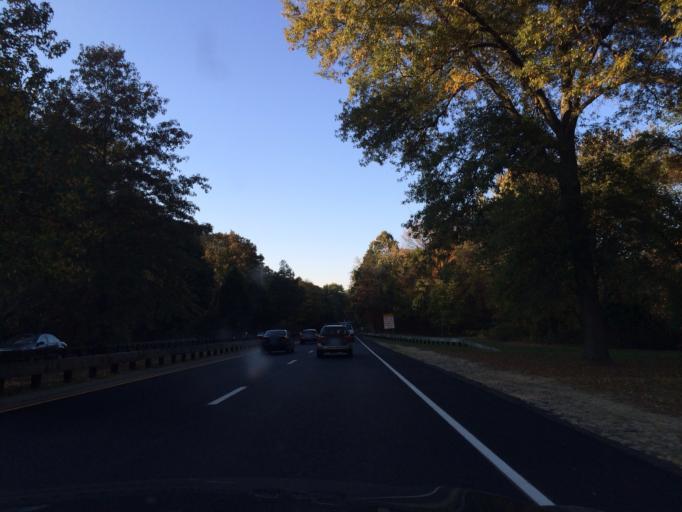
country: US
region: Connecticut
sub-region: Fairfield County
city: Glenville
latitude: 41.0489
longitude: -73.6710
